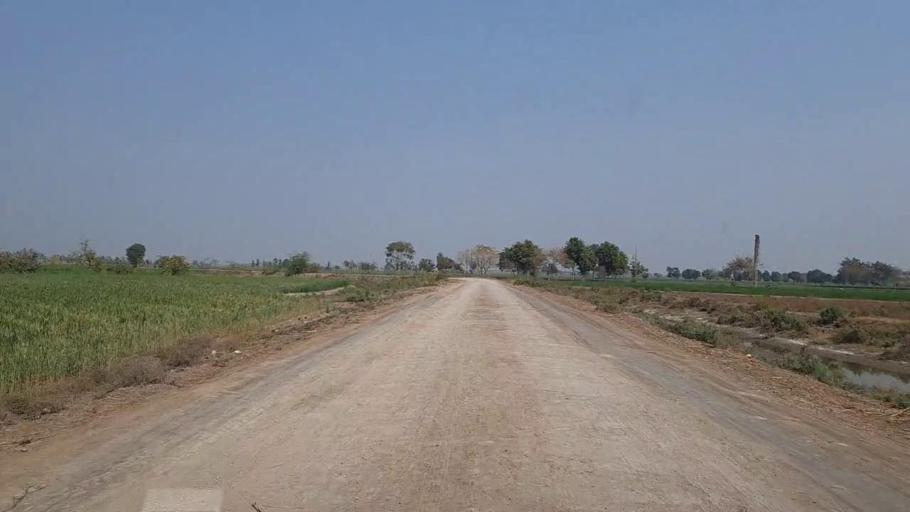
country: PK
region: Sindh
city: Mirwah Gorchani
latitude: 25.3157
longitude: 69.0606
